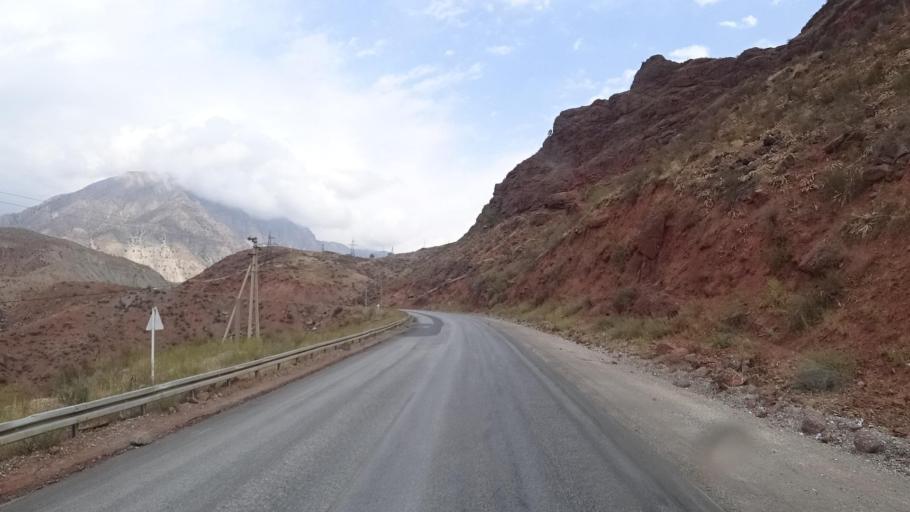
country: KG
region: Jalal-Abad
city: Toktogul
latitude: 41.6224
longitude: 72.6427
